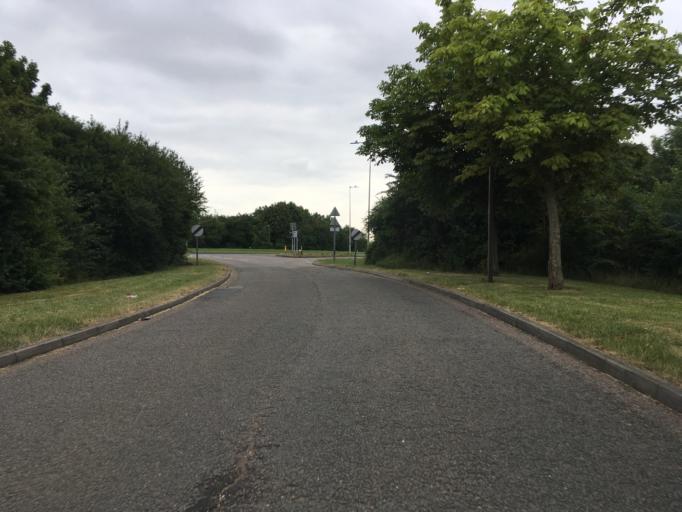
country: GB
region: England
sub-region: Milton Keynes
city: Broughton
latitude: 52.0391
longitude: -0.7010
